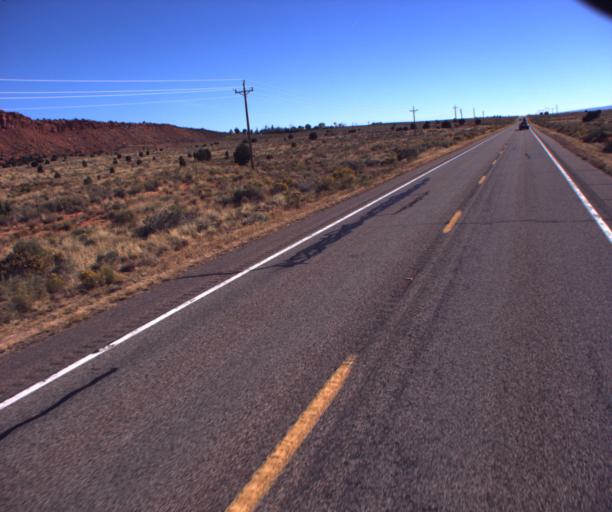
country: US
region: Arizona
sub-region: Coconino County
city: Fredonia
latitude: 36.8578
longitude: -112.7540
